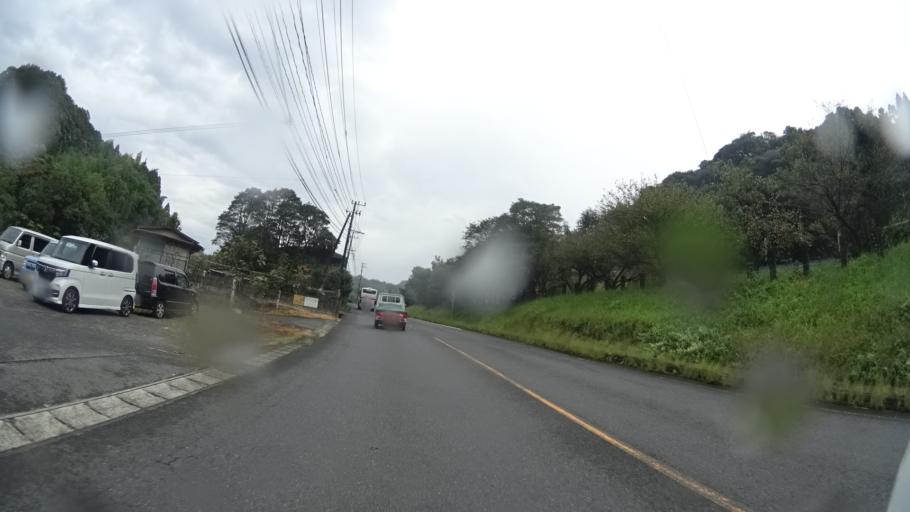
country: JP
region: Kagoshima
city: Kajiki
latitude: 31.7668
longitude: 130.6708
